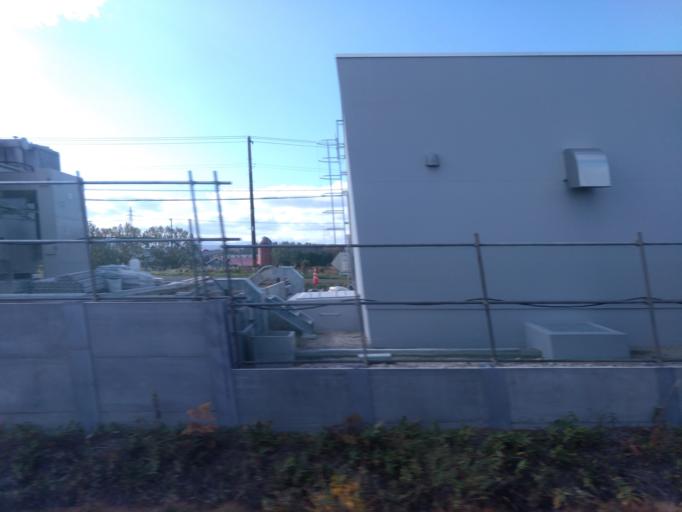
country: JP
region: Hokkaido
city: Kitahiroshima
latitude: 42.9087
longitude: 141.5741
